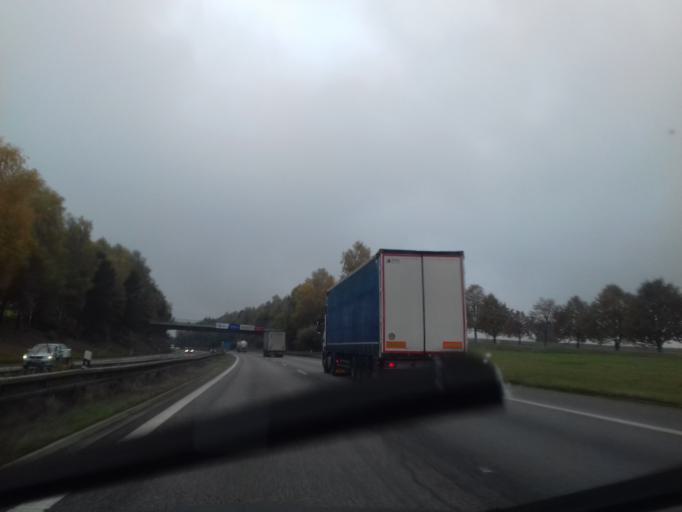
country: CZ
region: Vysocina
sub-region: Okres Pelhrimov
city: Humpolec
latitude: 49.5539
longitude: 15.3254
